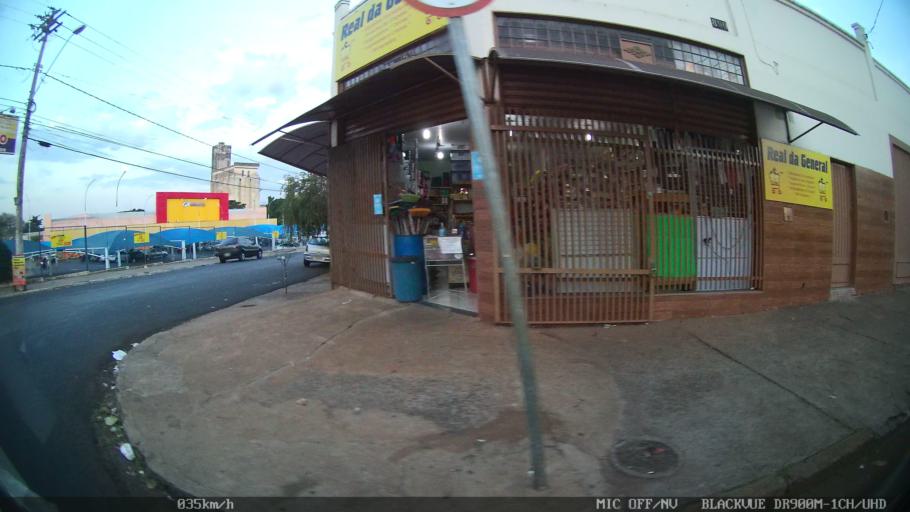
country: BR
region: Sao Paulo
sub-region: Ribeirao Preto
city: Ribeirao Preto
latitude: -21.1501
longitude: -47.8232
